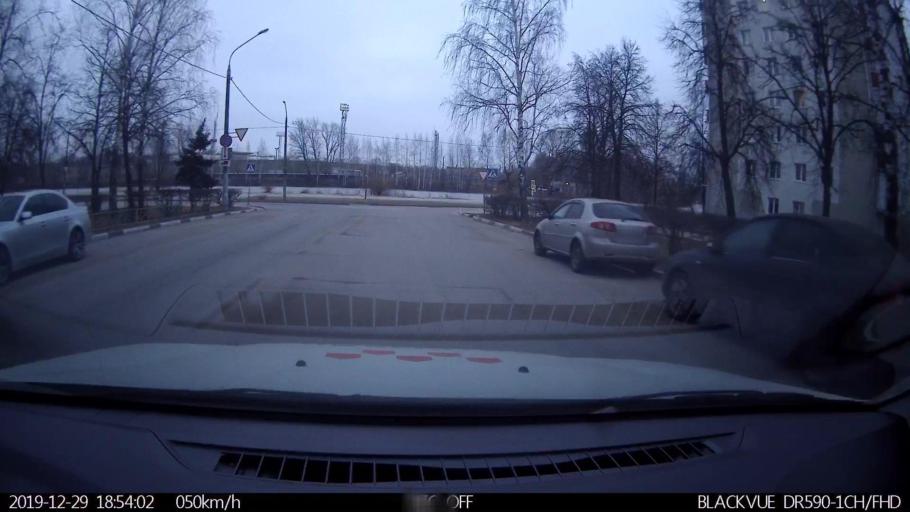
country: RU
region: Nizjnij Novgorod
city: Gorbatovka
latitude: 56.3459
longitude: 43.8530
